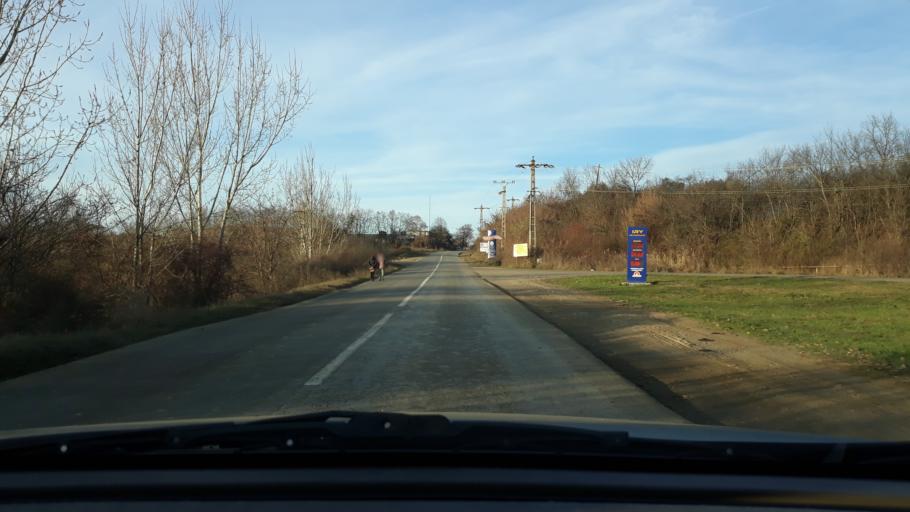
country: RO
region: Bihor
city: Foglas
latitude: 47.2458
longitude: 22.5338
